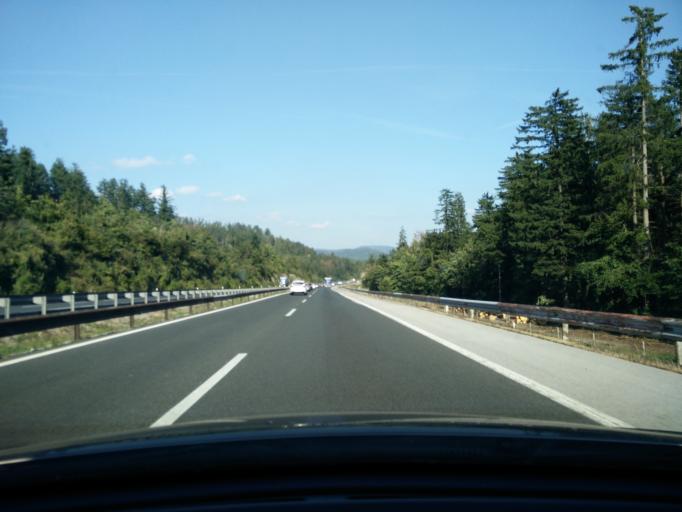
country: SI
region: Cerknica
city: Rakek
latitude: 45.8014
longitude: 14.2636
